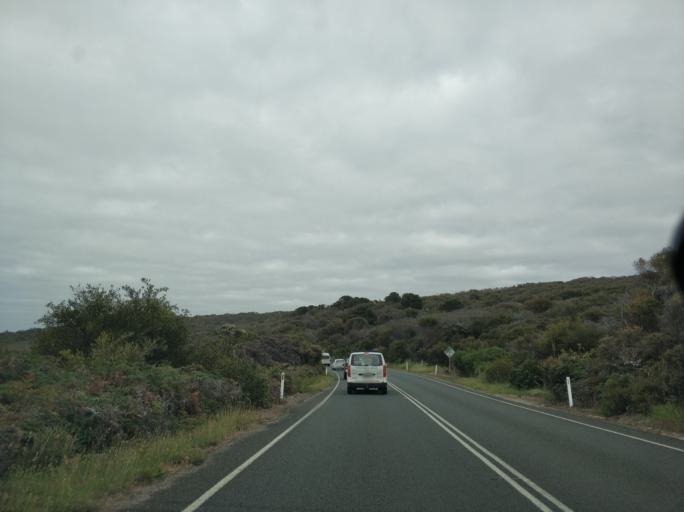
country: AU
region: Victoria
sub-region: Surf Coast
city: Anglesea
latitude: -38.4323
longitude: 144.1359
